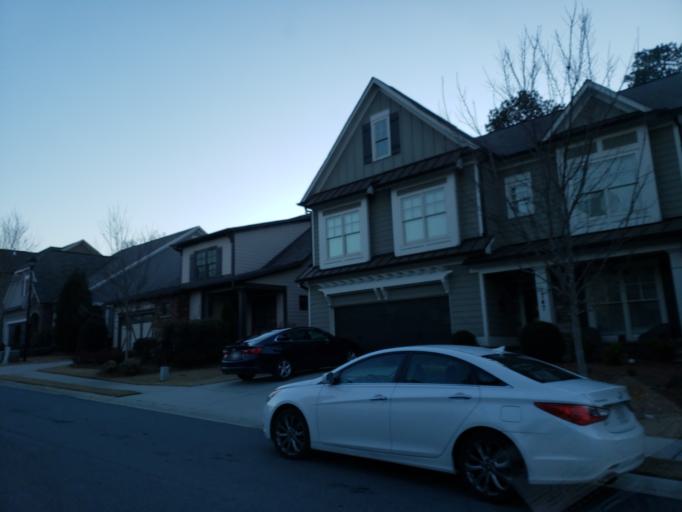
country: US
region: Georgia
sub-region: Cherokee County
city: Woodstock
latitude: 34.0971
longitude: -84.4948
